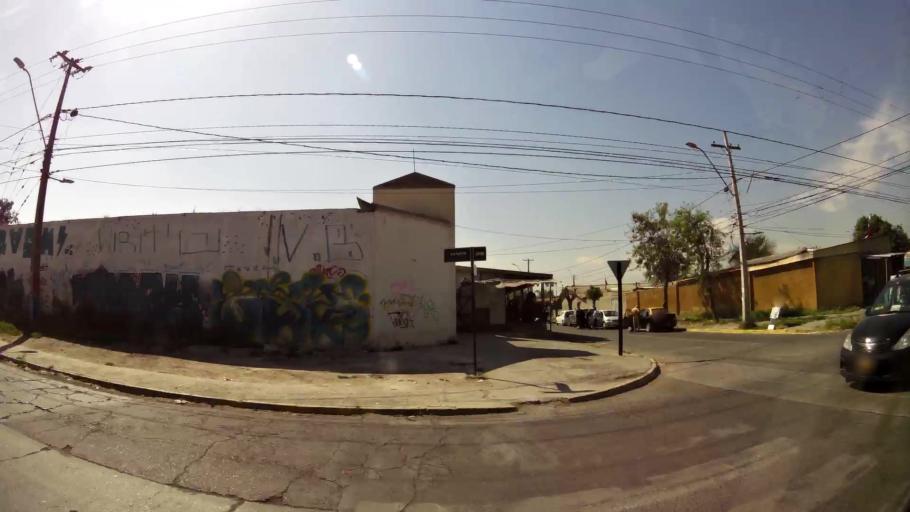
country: CL
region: Santiago Metropolitan
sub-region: Provincia de Maipo
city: San Bernardo
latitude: -33.5881
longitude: -70.6945
